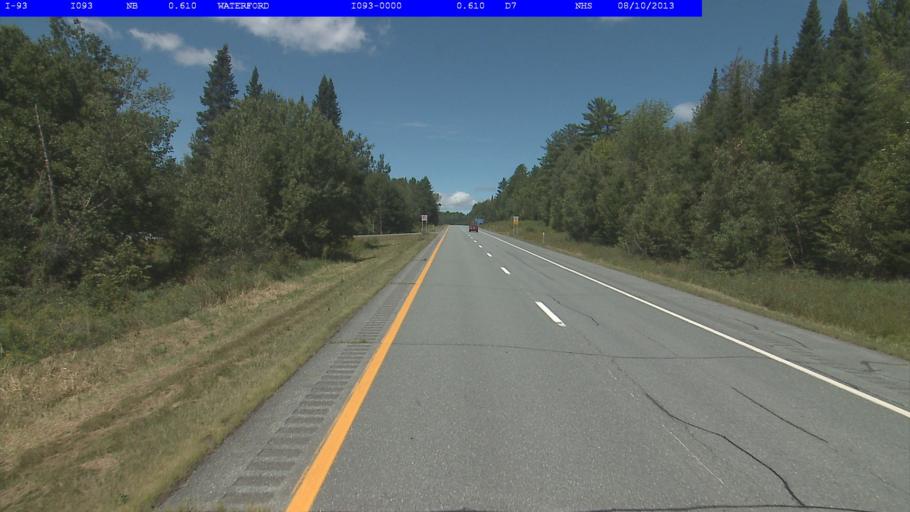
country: US
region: New Hampshire
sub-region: Grafton County
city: Littleton
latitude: 44.3517
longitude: -71.8942
